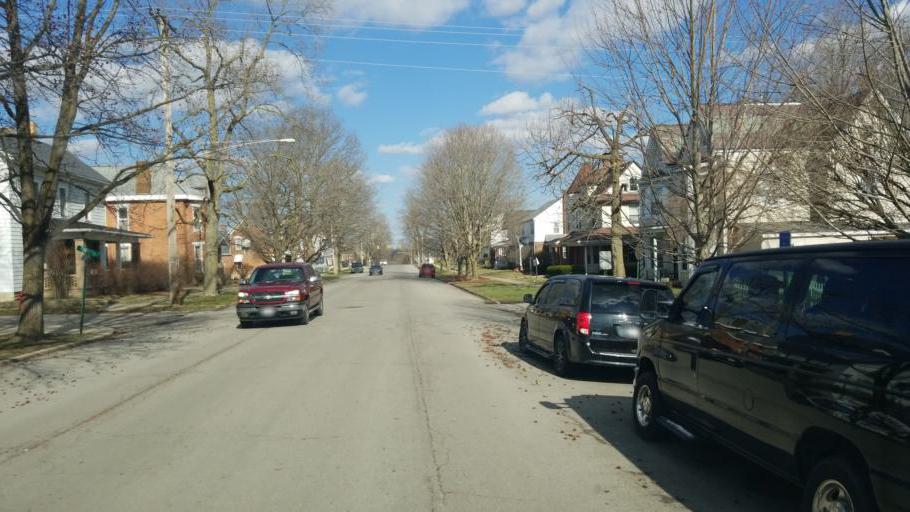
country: US
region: Ohio
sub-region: Highland County
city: Greenfield
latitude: 39.3489
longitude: -83.3845
